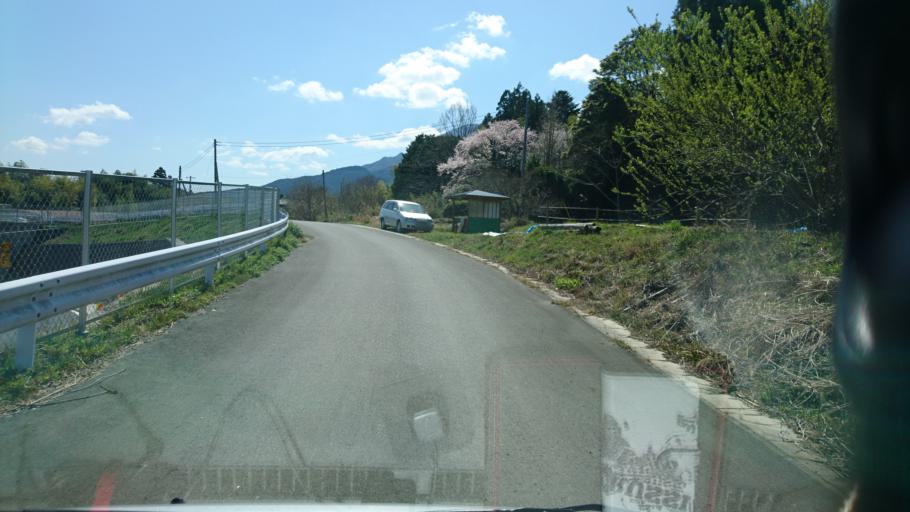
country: JP
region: Shizuoka
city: Fujinomiya
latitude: 35.3032
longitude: 138.4461
